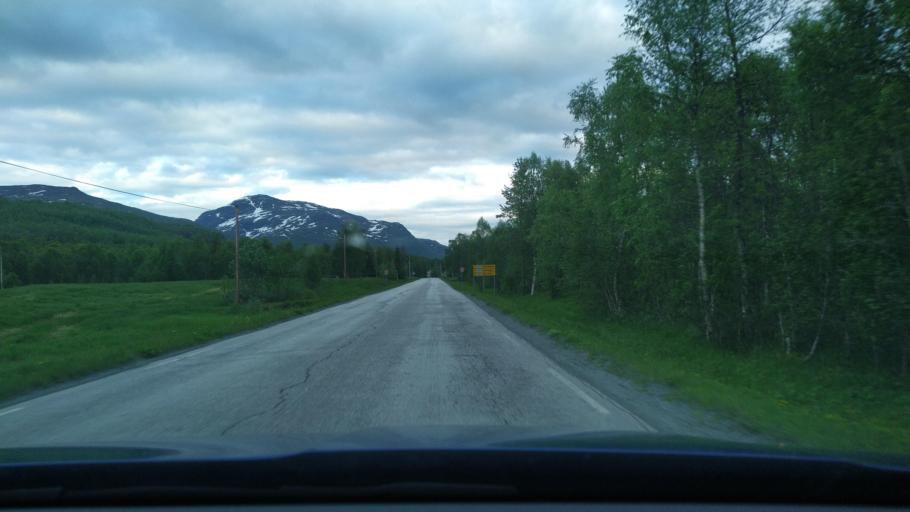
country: NO
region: Troms
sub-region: Dyroy
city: Brostadbotn
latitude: 69.0660
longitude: 17.7355
